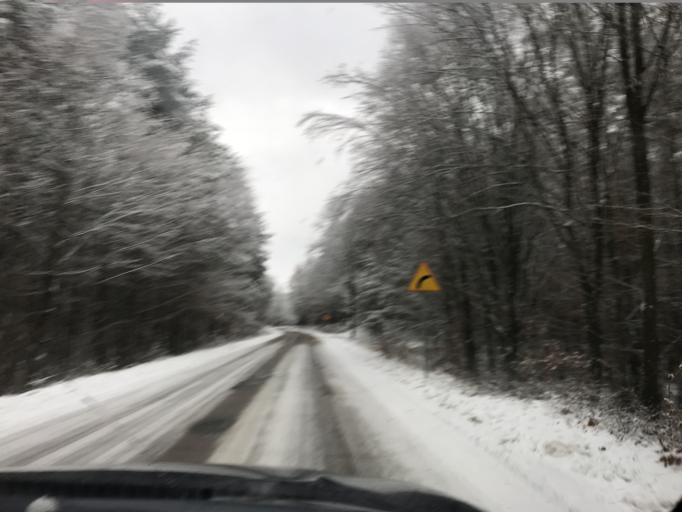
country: PL
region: Pomeranian Voivodeship
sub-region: Powiat bytowski
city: Parchowo
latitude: 54.2537
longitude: 17.5806
